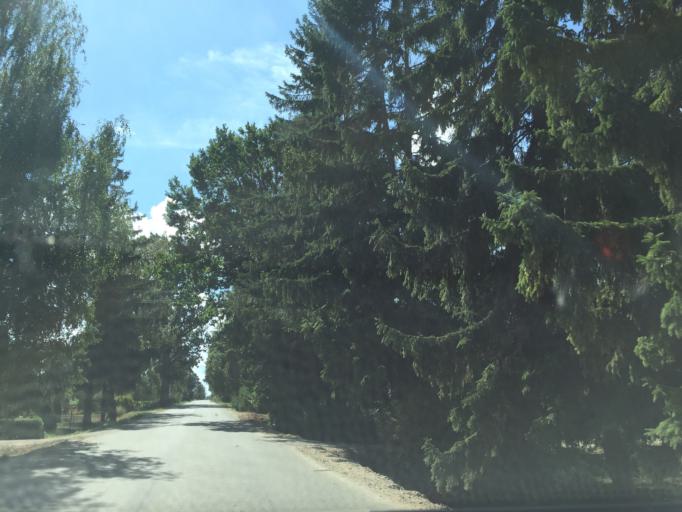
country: LV
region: Rundales
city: Pilsrundale
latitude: 56.3153
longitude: 23.9114
